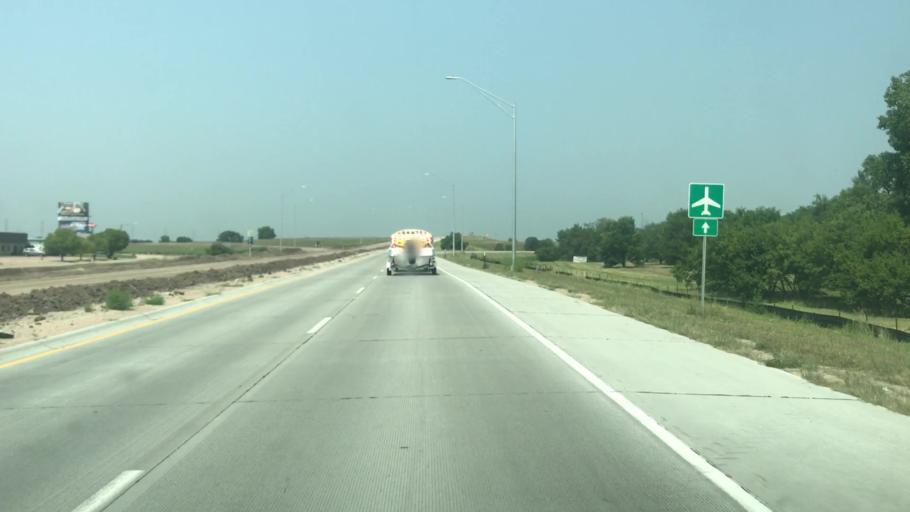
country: US
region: Nebraska
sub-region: Hall County
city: Grand Island
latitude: 40.9485
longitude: -98.3837
